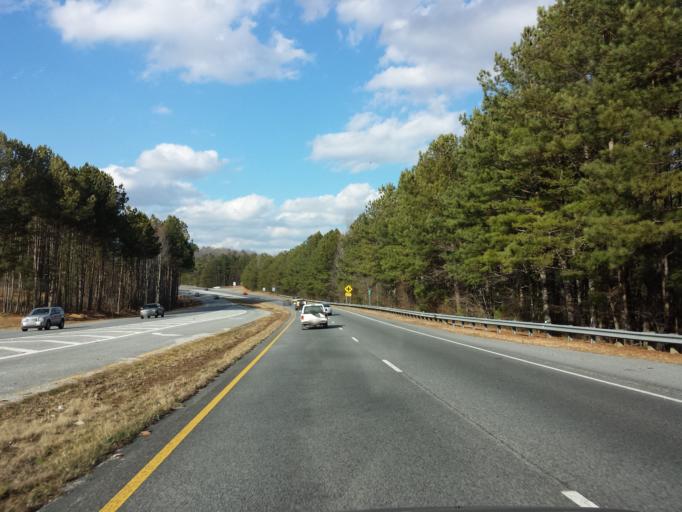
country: US
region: Georgia
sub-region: Lumpkin County
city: Dahlonega
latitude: 34.4236
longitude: -83.9909
